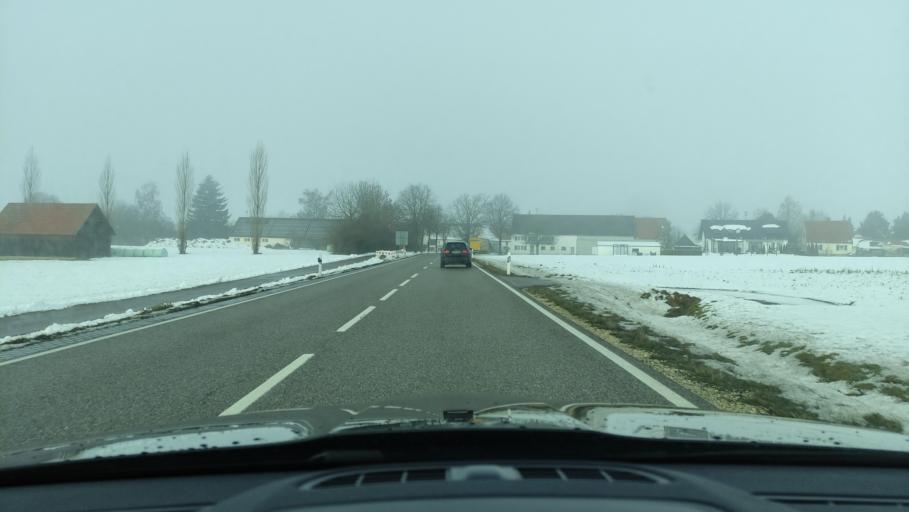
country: DE
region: Bavaria
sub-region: Swabia
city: Deisenhausen
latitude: 48.2820
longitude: 10.3352
